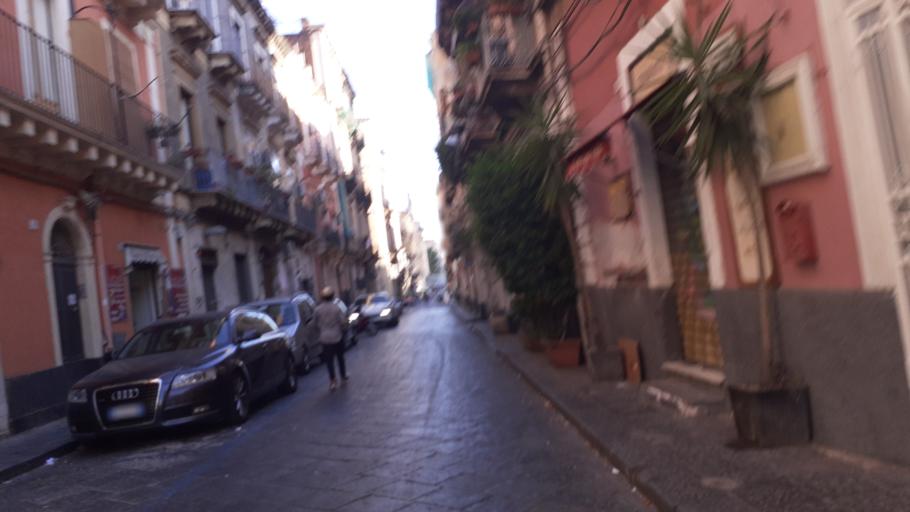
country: IT
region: Sicily
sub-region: Catania
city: Catania
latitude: 37.5121
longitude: 15.0881
